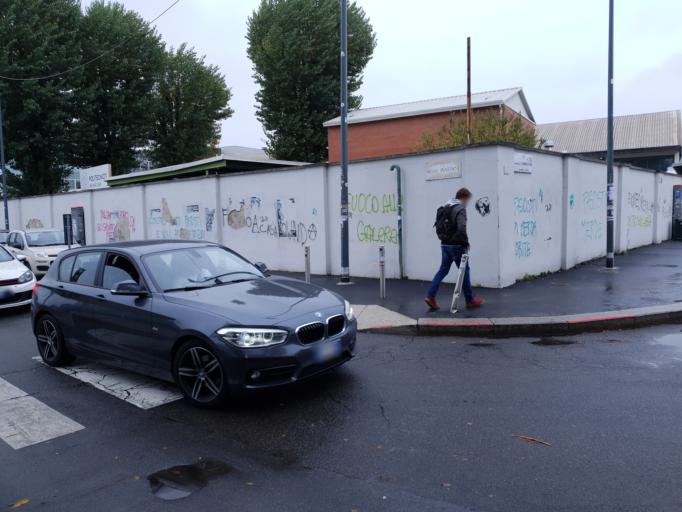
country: IT
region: Lombardy
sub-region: Citta metropolitana di Milano
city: Novate Milanese
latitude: 45.5023
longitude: 9.1586
